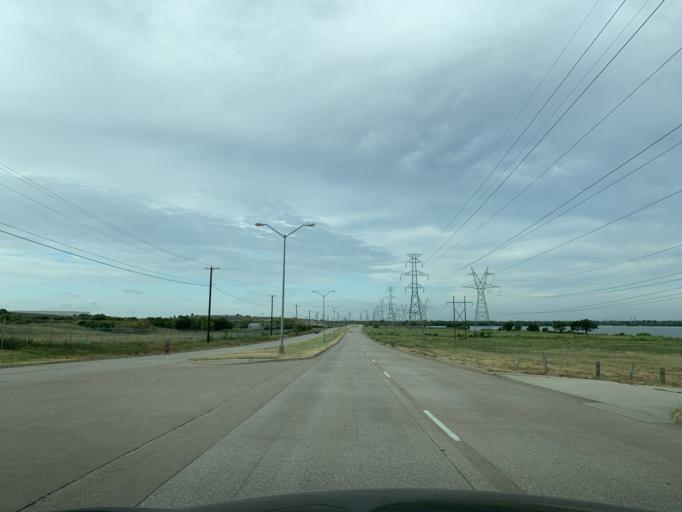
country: US
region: Texas
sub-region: Dallas County
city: Grand Prairie
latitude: 32.7052
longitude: -96.9544
